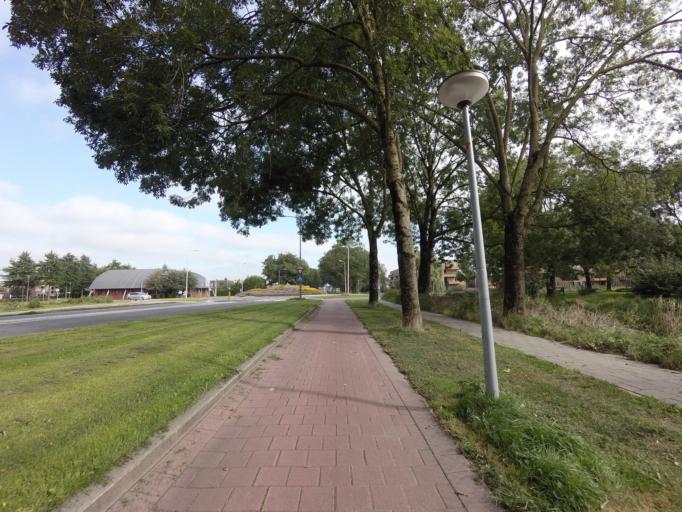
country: NL
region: Overijssel
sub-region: Gemeente Steenwijkerland
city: Steenwijk
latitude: 52.7936
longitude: 6.1228
